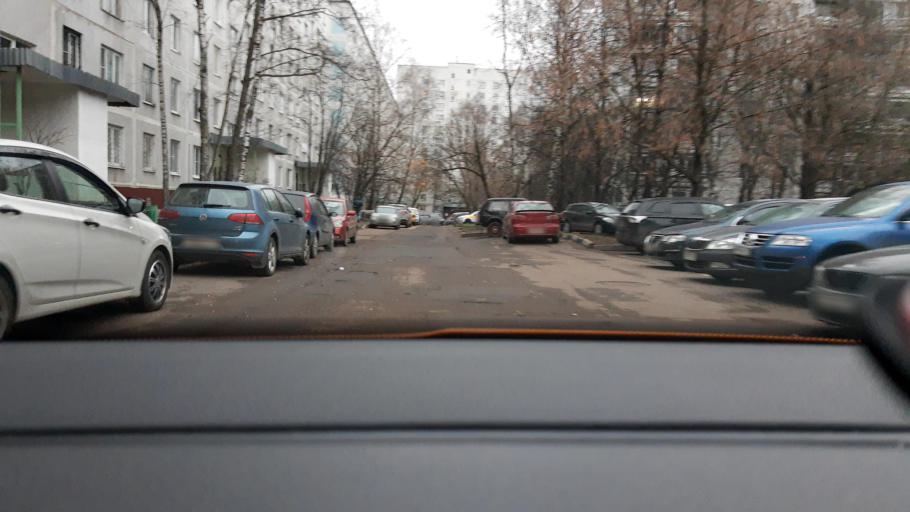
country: RU
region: Moscow
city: Bibirevo
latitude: 55.8961
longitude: 37.6283
